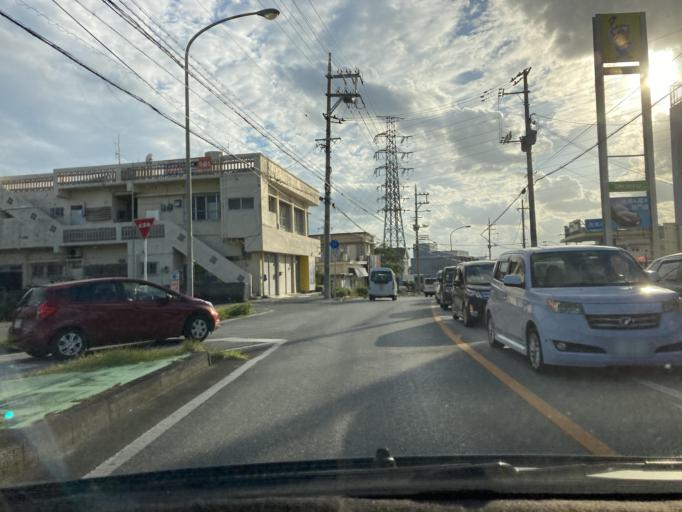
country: JP
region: Okinawa
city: Okinawa
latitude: 26.3221
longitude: 127.7888
